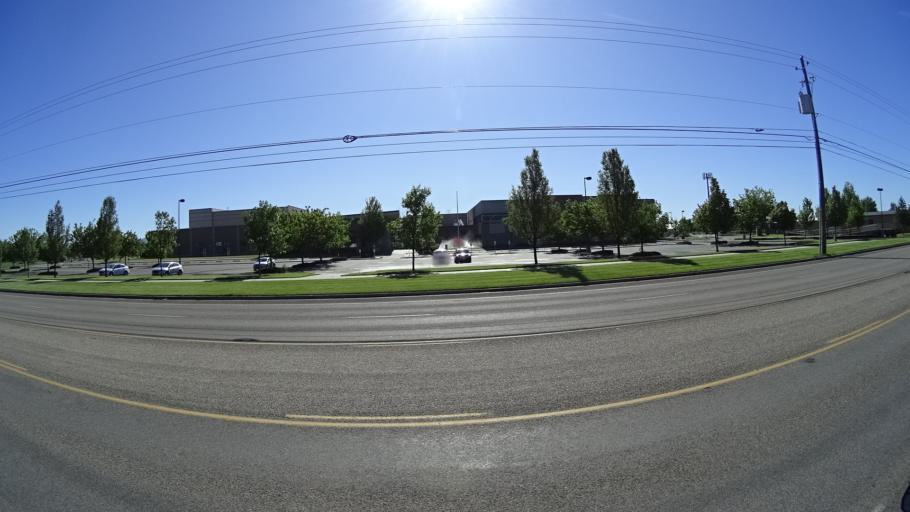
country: US
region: Idaho
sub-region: Ada County
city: Meridian
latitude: 43.6537
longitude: -116.4137
